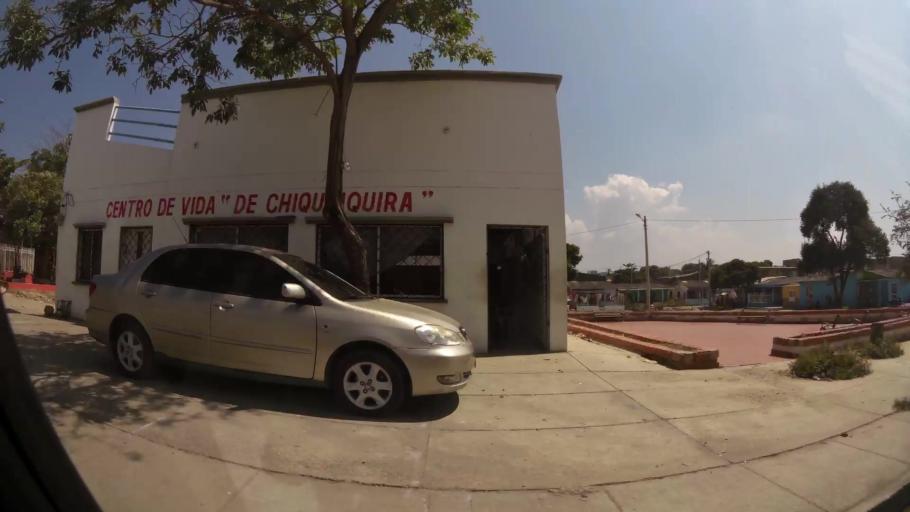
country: CO
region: Bolivar
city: Cartagena
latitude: 10.4050
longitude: -75.4917
